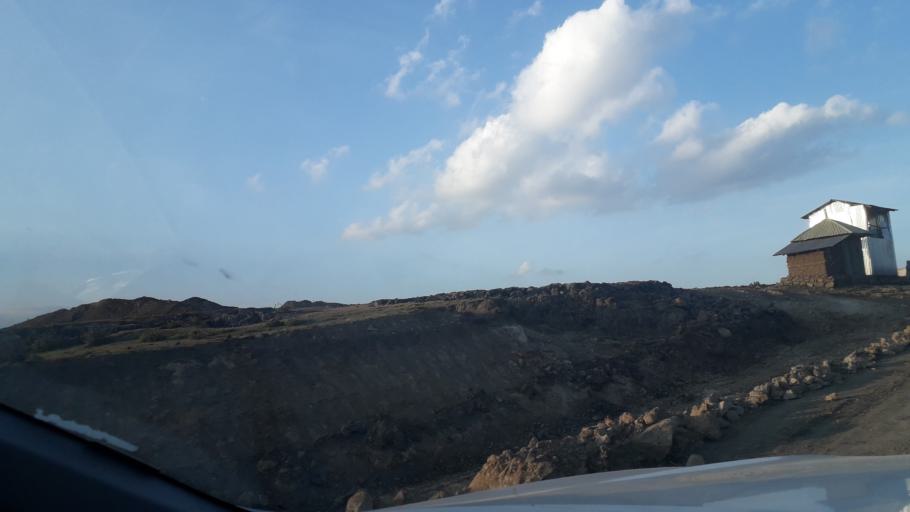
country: ET
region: Amhara
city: Lalibela
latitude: 11.5532
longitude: 39.2226
